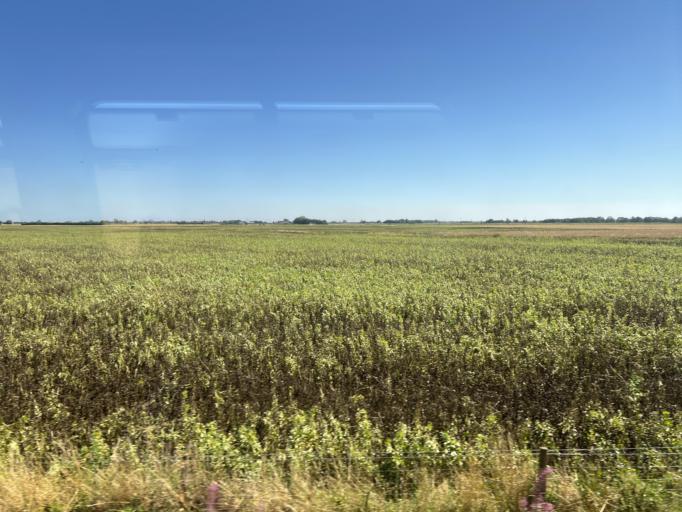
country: GB
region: England
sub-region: Lincolnshire
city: Spilsby
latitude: 53.1226
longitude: 0.1394
